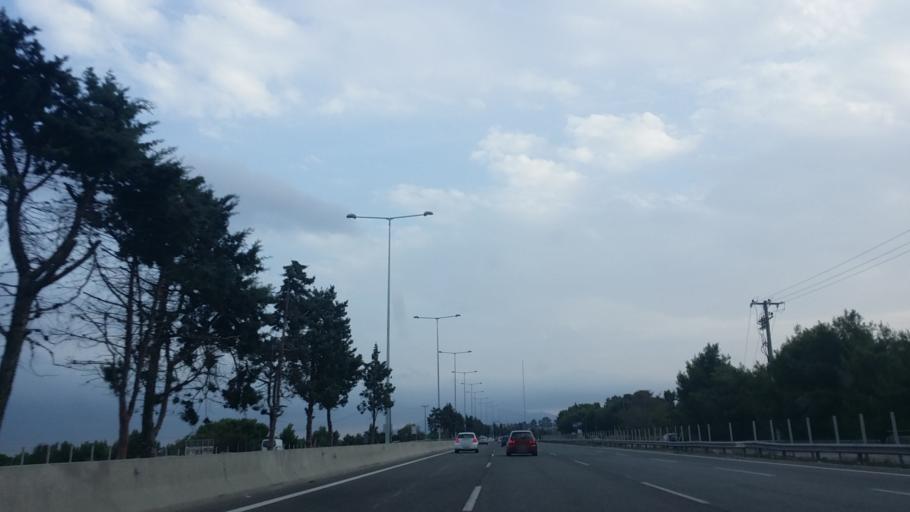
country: GR
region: Attica
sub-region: Nomarchia Anatolikis Attikis
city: Agios Stefanos
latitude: 38.1719
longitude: 23.8550
